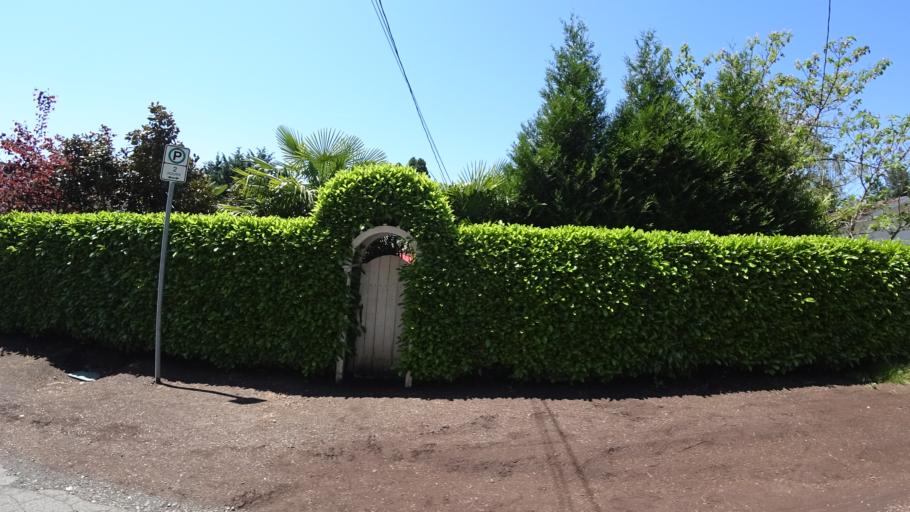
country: US
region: Oregon
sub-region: Multnomah County
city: Portland
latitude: 45.4738
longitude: -122.6836
